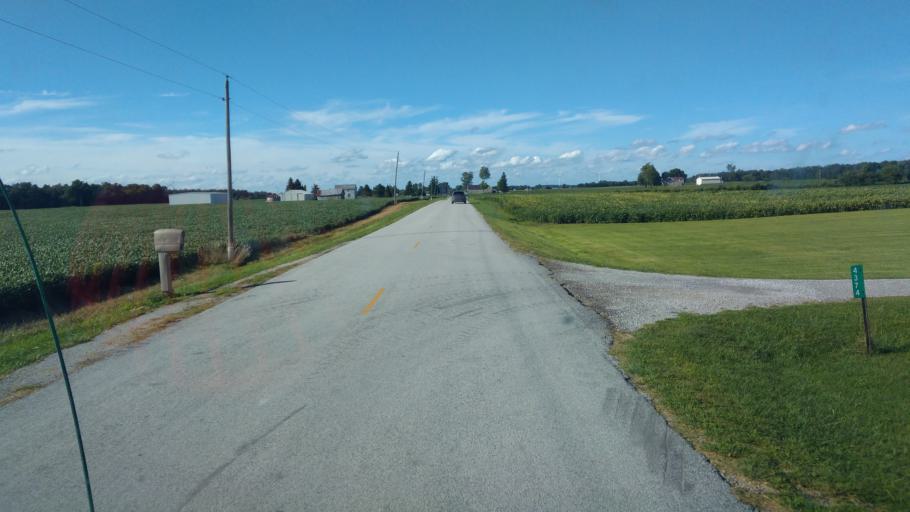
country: US
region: Ohio
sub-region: Hardin County
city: Ada
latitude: 40.7560
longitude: -83.6905
